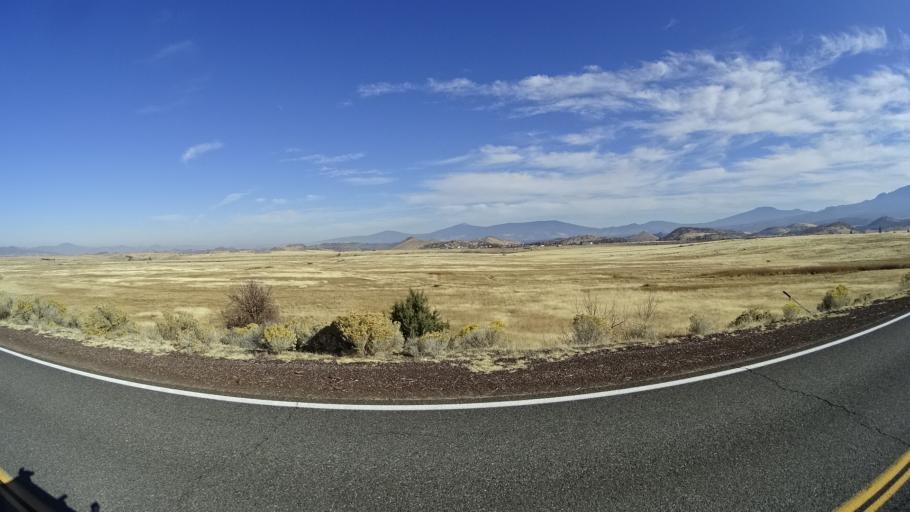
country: US
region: California
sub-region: Siskiyou County
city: Weed
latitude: 41.4674
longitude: -122.4685
